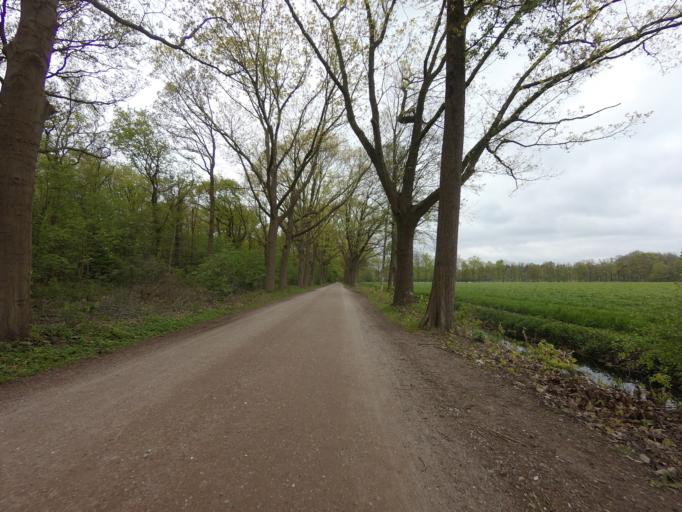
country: NL
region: Utrecht
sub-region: Gemeente De Bilt
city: De Bilt
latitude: 52.1280
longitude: 5.1680
